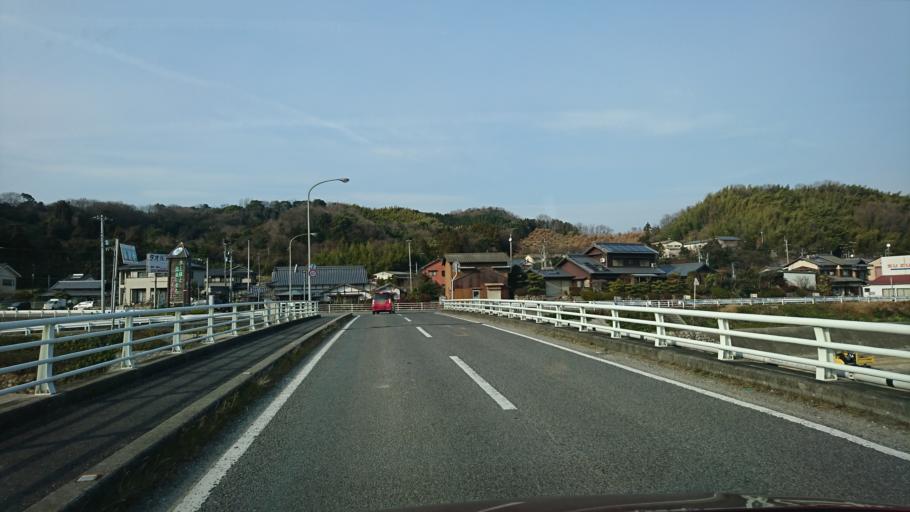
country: JP
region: Ehime
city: Hojo
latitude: 34.0269
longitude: 132.9599
